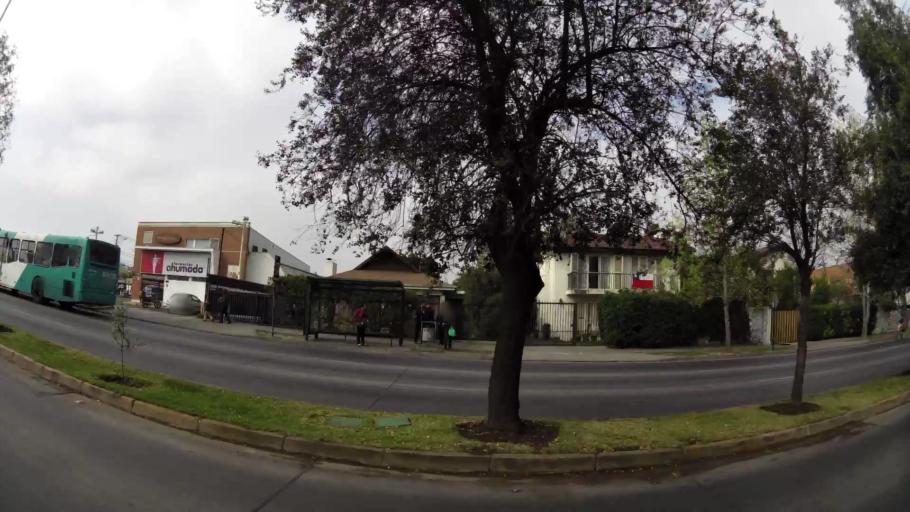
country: CL
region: Santiago Metropolitan
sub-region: Provincia de Santiago
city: Villa Presidente Frei, Nunoa, Santiago, Chile
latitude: -33.4305
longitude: -70.5553
